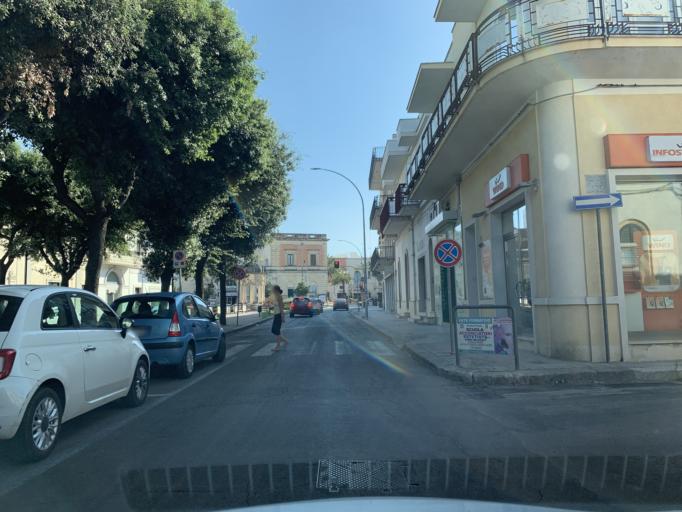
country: IT
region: Apulia
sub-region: Provincia di Lecce
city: Nardo
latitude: 40.1804
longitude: 18.0341
